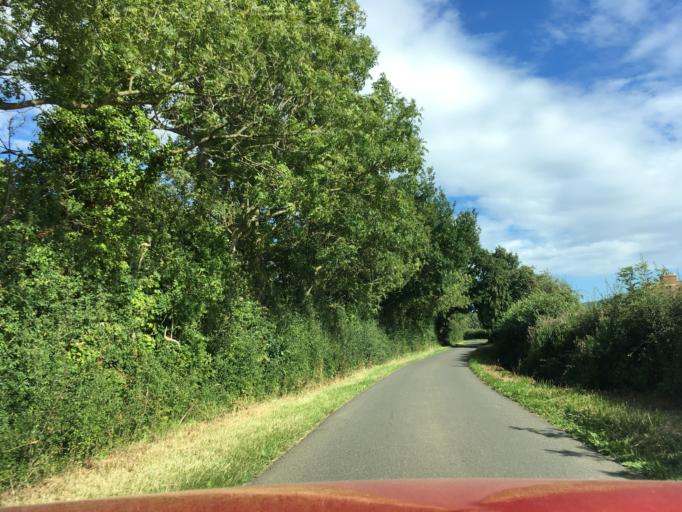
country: GB
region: England
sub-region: Gloucestershire
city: Stonehouse
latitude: 51.8009
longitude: -2.2637
